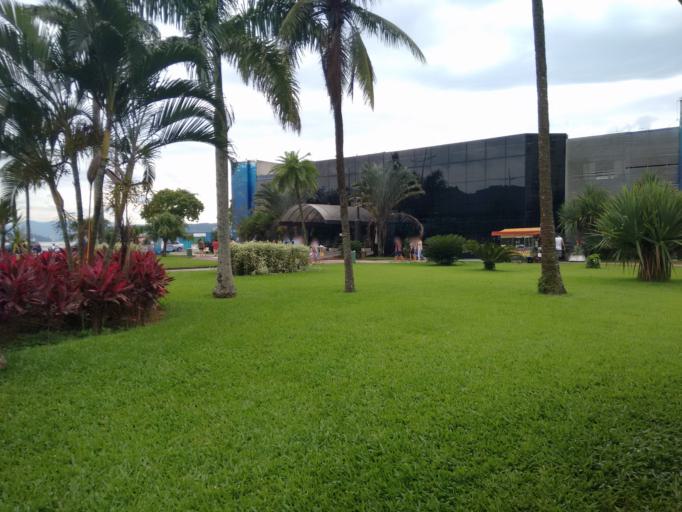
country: BR
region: Sao Paulo
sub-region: Santos
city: Santos
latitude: -23.9868
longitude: -46.3080
